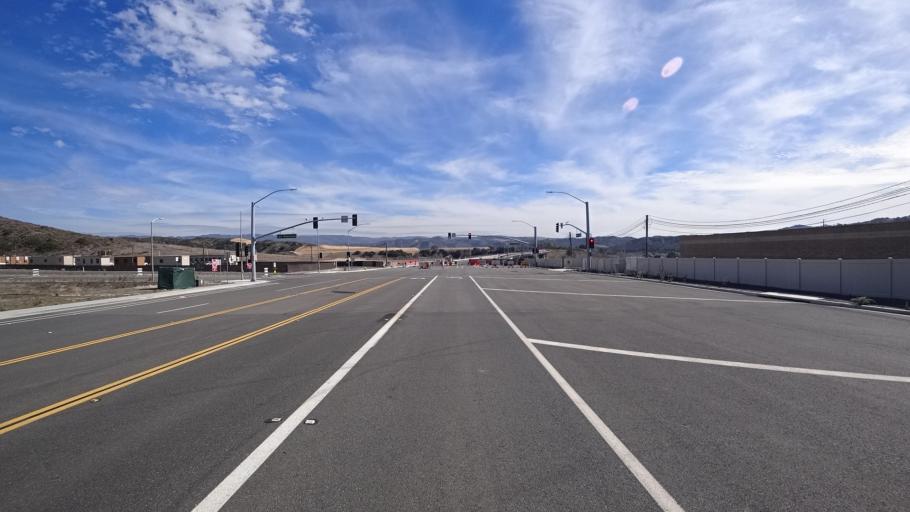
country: US
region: California
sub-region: Orange County
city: Ladera Ranch
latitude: 33.5269
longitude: -117.5985
